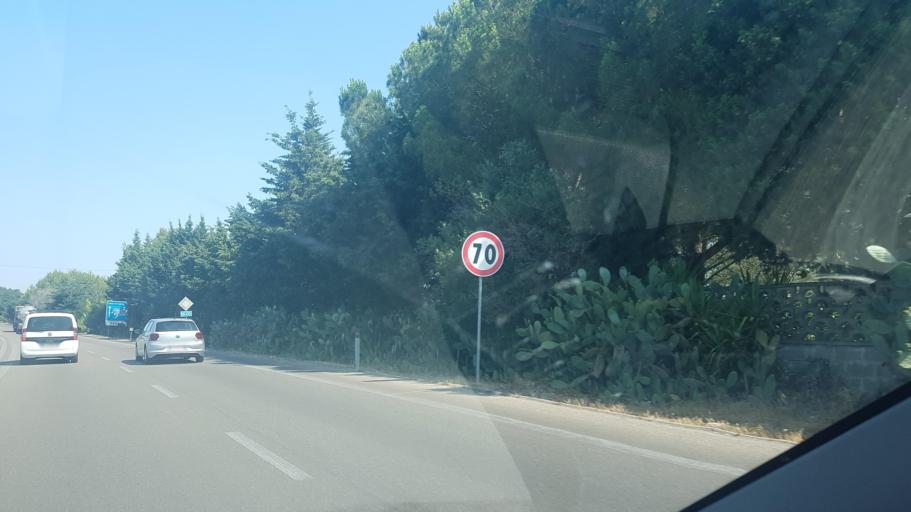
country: IT
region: Apulia
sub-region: Provincia di Lecce
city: Maglie
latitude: 40.1186
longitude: 18.3199
